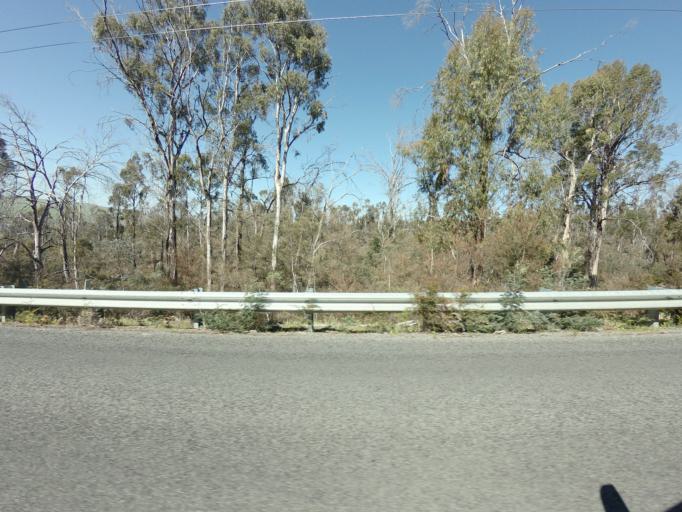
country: AU
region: Tasmania
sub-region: Derwent Valley
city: New Norfolk
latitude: -42.5439
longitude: 146.7175
